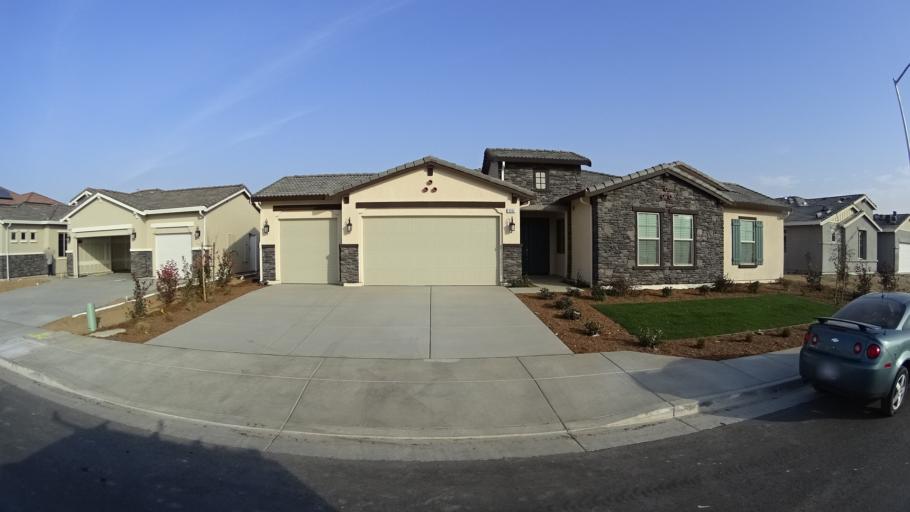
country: US
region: California
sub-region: Kern County
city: Greenacres
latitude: 35.4328
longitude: -119.1047
